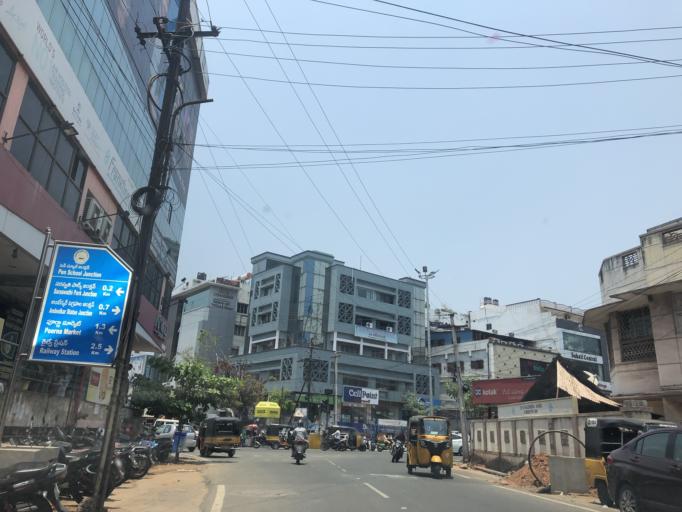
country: IN
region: Andhra Pradesh
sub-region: Vishakhapatnam
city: Yarada
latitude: 17.7149
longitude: 83.3022
